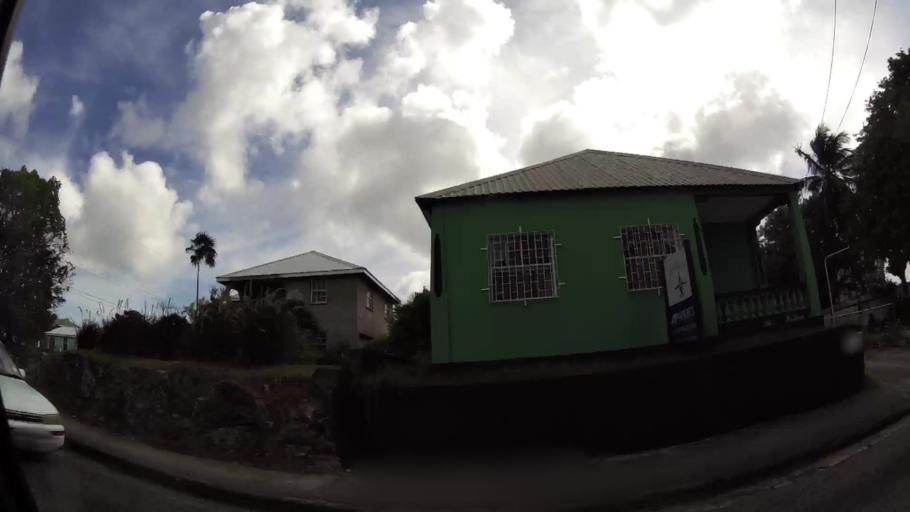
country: BB
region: Saint Michael
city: Bridgetown
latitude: 13.0935
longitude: -59.5950
